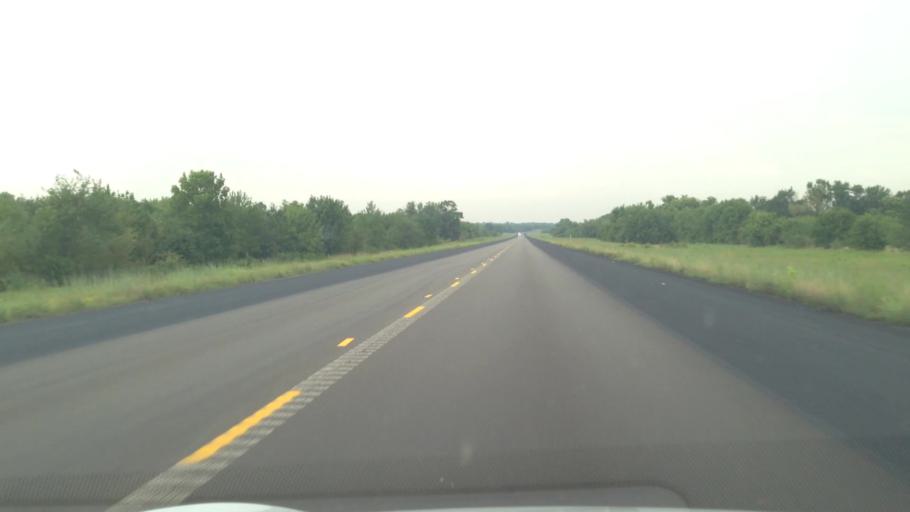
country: US
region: Kansas
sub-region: Cherokee County
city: Baxter Springs
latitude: 37.0415
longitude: -94.7103
